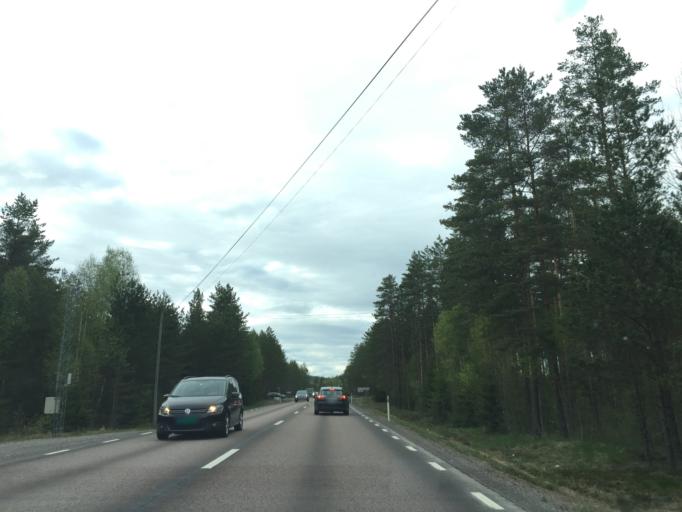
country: SE
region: Vaermland
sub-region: Eda Kommun
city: Charlottenberg
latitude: 59.9104
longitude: 12.2748
